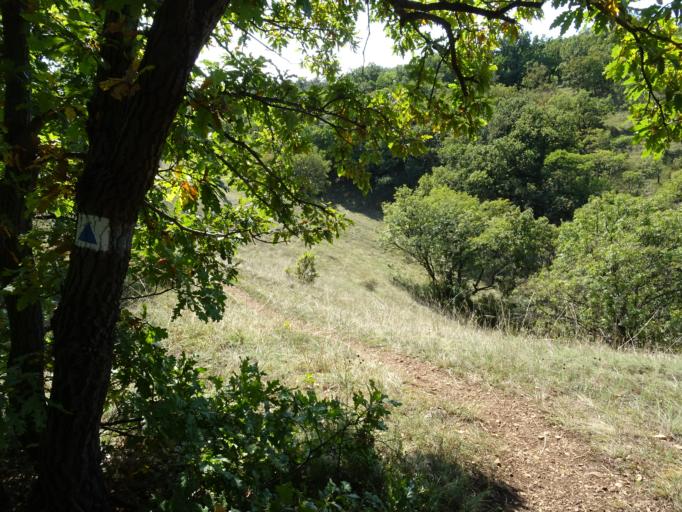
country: HU
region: Fejer
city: Zamoly
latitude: 47.3798
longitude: 18.3838
